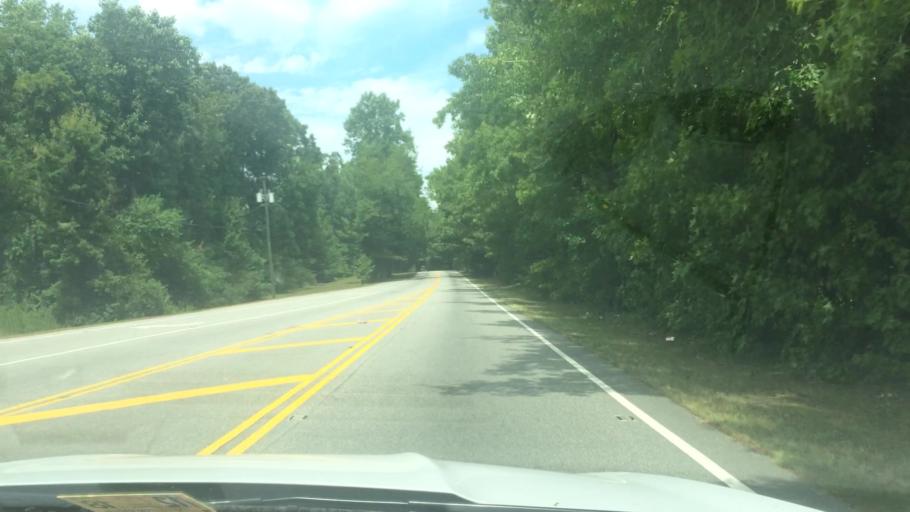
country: US
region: Virginia
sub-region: York County
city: Yorktown
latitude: 37.2016
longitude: -76.5791
